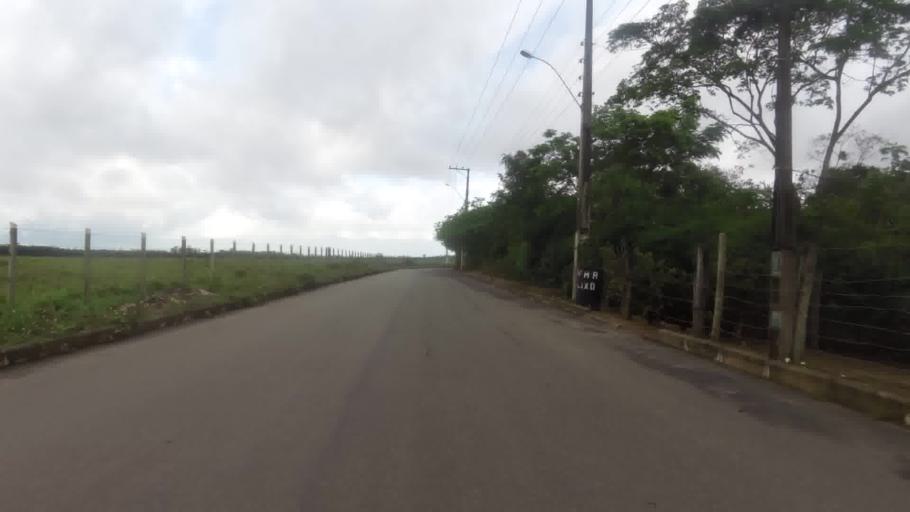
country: BR
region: Espirito Santo
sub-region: Piuma
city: Piuma
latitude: -20.7689
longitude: -40.6301
